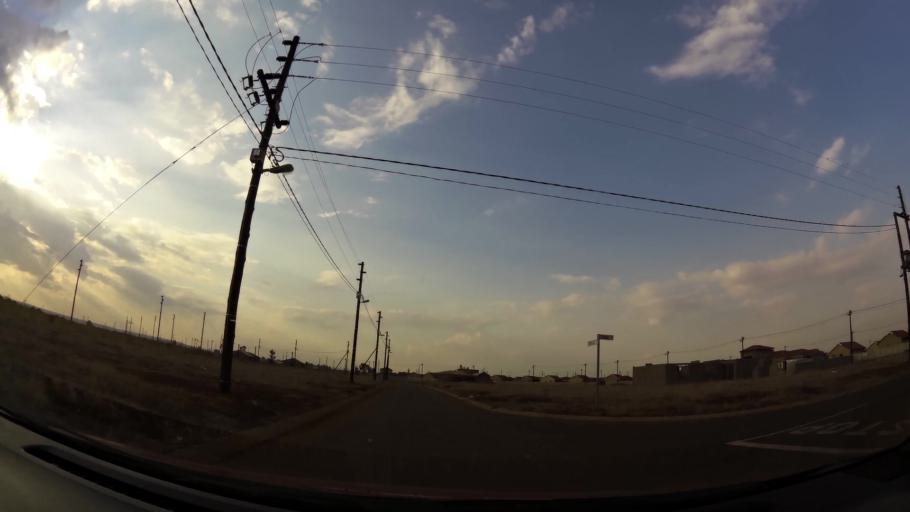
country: ZA
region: Gauteng
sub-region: Sedibeng District Municipality
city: Vanderbijlpark
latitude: -26.6119
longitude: 27.8110
